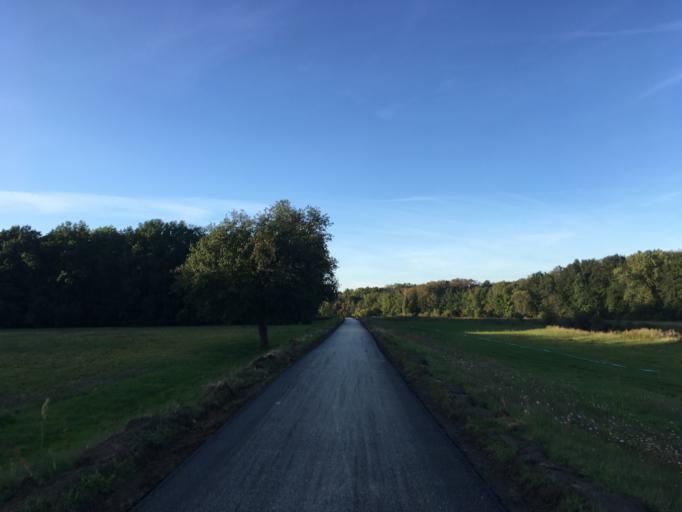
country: DE
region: Brandenburg
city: Forst
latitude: 51.7197
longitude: 14.6781
